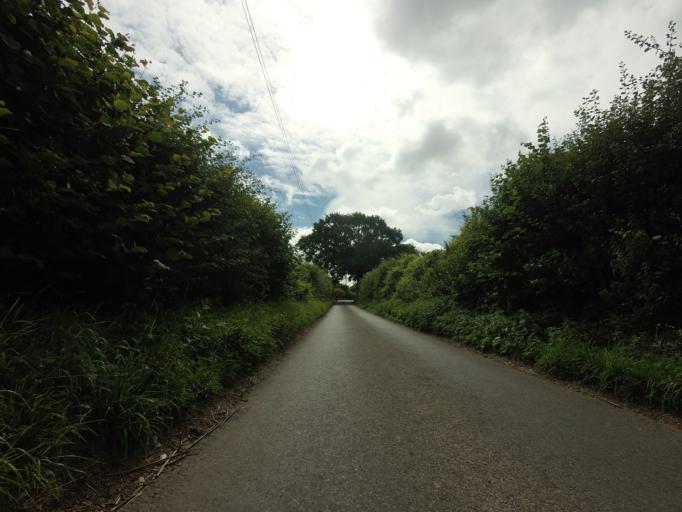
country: GB
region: England
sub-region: Kent
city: Swanley
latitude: 51.3663
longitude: 0.1487
